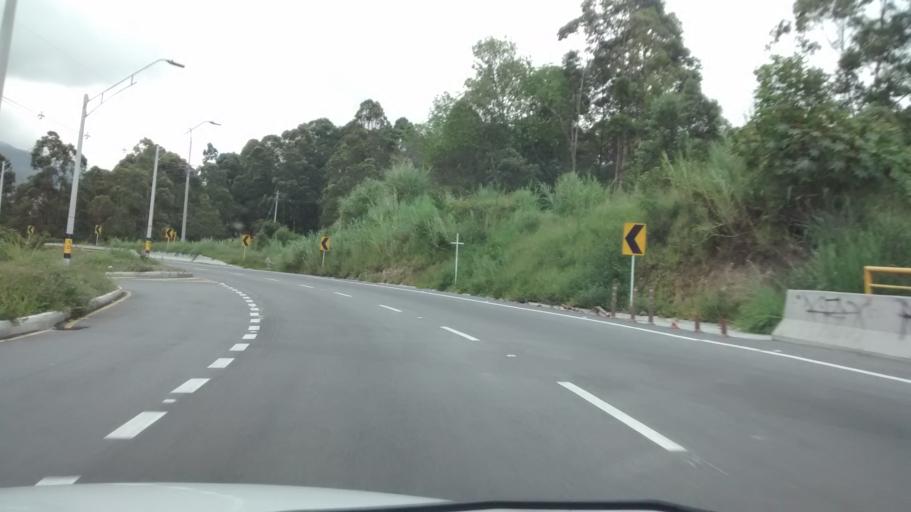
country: CO
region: Antioquia
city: Medellin
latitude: 6.2746
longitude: -75.6218
